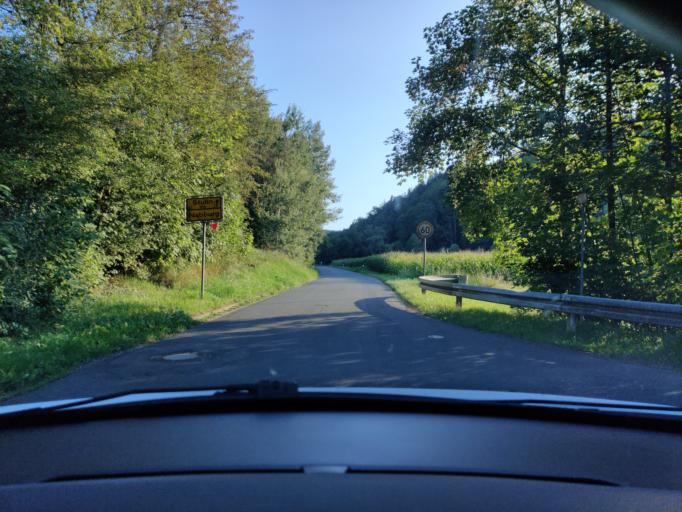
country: DE
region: Bavaria
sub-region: Upper Palatinate
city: Nabburg
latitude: 49.4429
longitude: 12.1756
